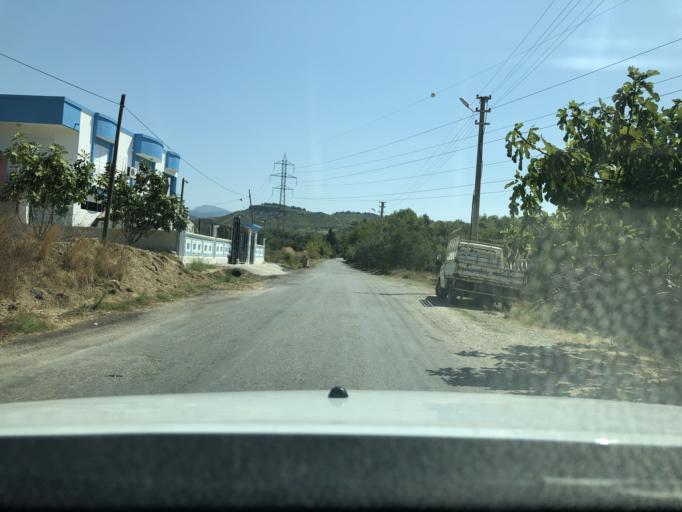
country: TR
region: Antalya
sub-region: Manavgat
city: Manavgat
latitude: 36.8216
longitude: 31.5029
